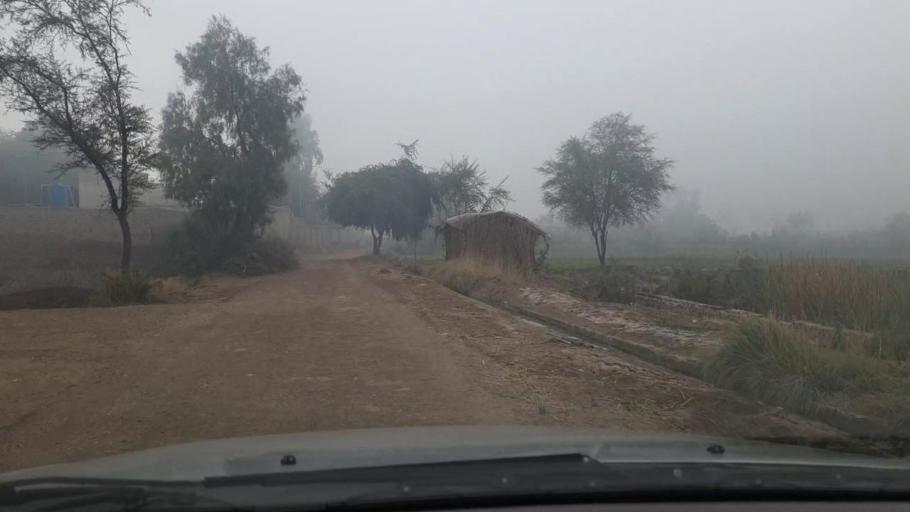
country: PK
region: Sindh
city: Khanpur
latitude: 27.8488
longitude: 69.4871
